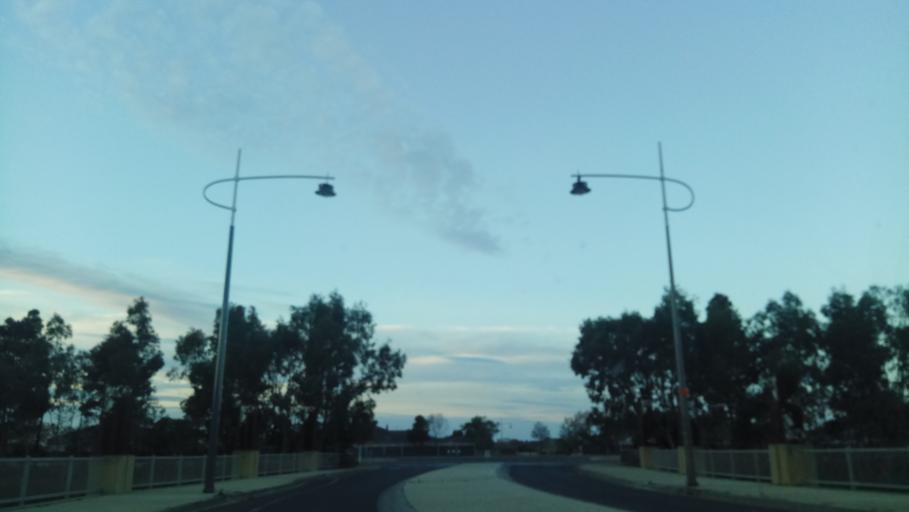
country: AU
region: Victoria
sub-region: Wyndham
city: Point Cook
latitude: -37.8997
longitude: 144.7420
